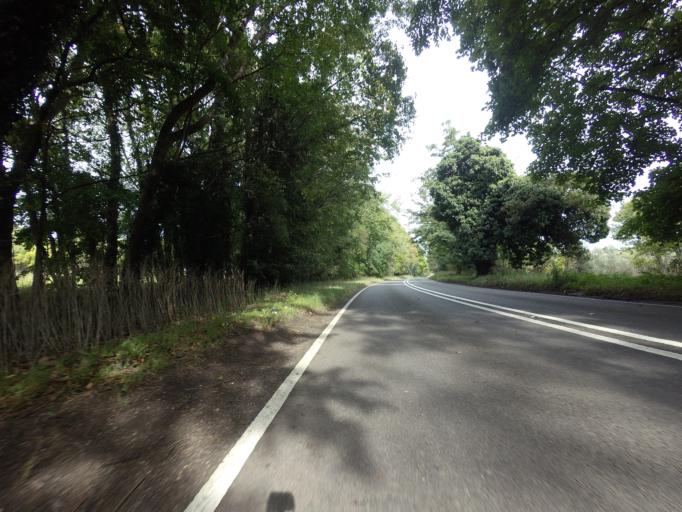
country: GB
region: England
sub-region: Essex
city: Saffron Walden
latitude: 52.0185
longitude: 0.2123
